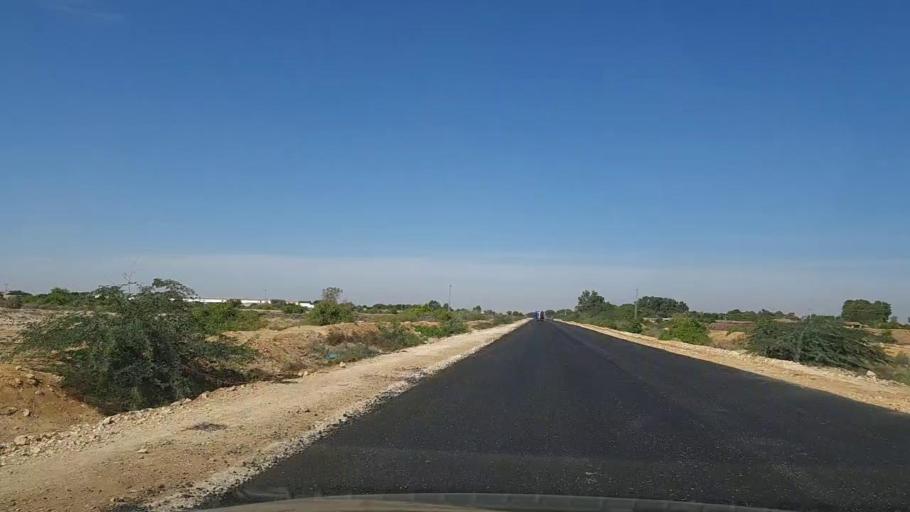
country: PK
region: Sindh
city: Kotri
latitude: 25.2283
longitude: 68.2356
